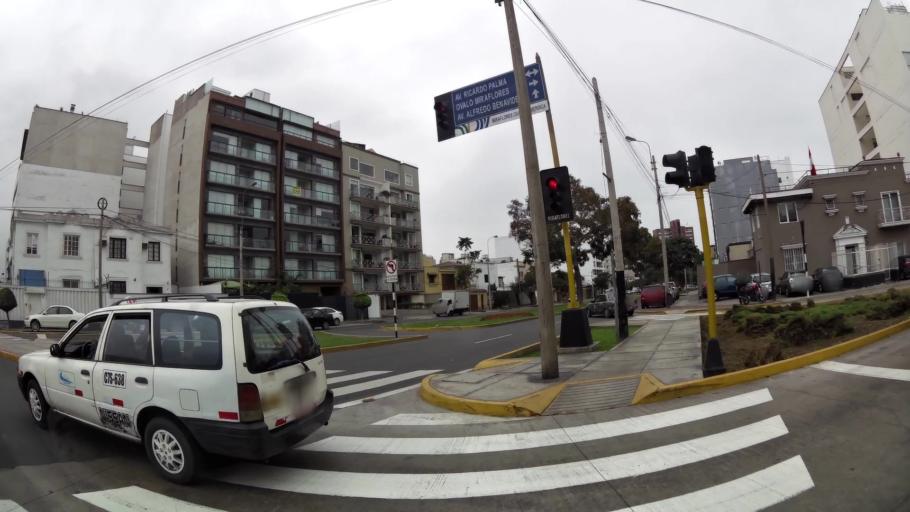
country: PE
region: Lima
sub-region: Lima
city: Surco
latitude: -12.1224
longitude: -77.0207
